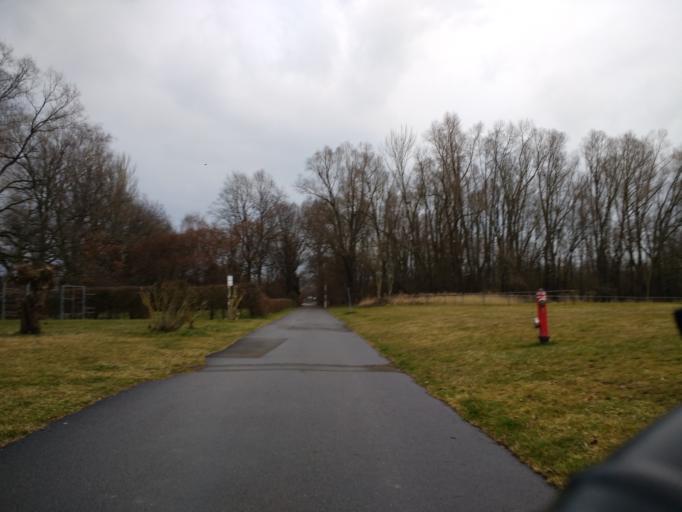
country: DE
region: Baden-Wuerttemberg
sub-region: Tuebingen Region
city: Uberlingen
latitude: 47.7469
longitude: 9.1491
